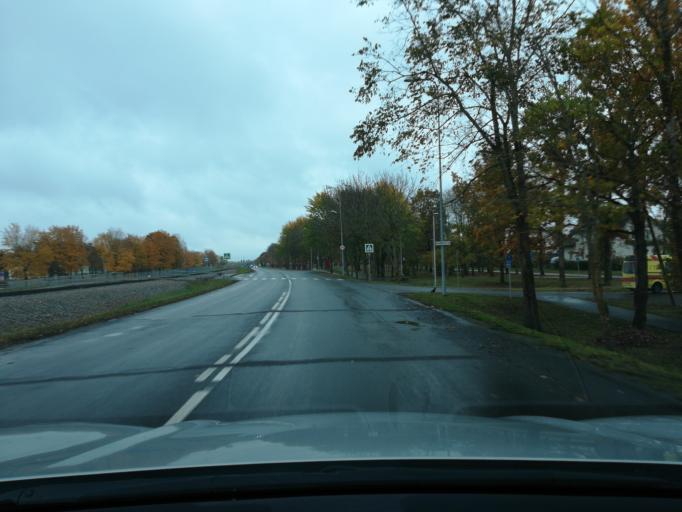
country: EE
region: Ida-Virumaa
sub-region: Johvi vald
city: Johvi
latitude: 59.3249
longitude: 27.4206
